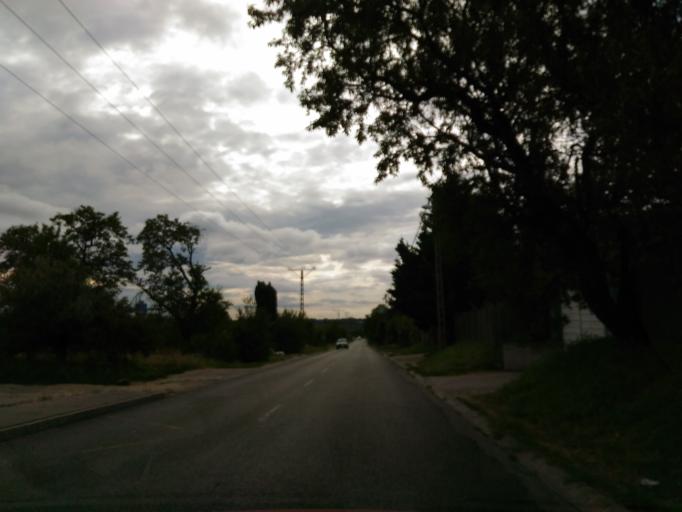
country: HU
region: Pest
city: Diosd
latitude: 47.4046
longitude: 18.9667
